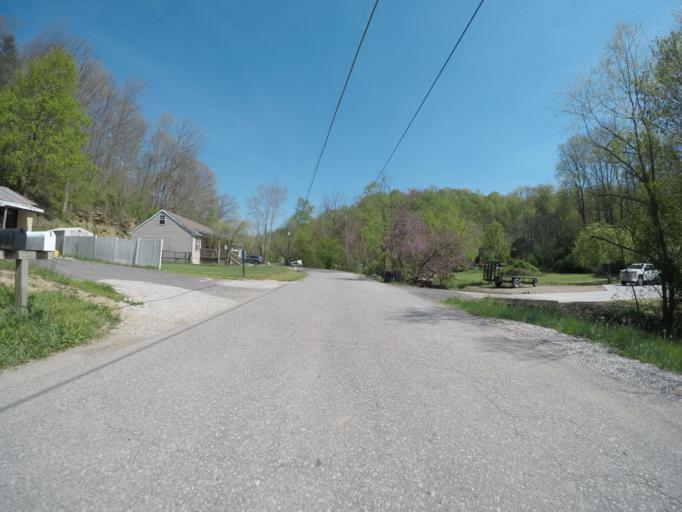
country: US
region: West Virginia
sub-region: Kanawha County
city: Charleston
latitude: 38.4175
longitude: -81.5825
